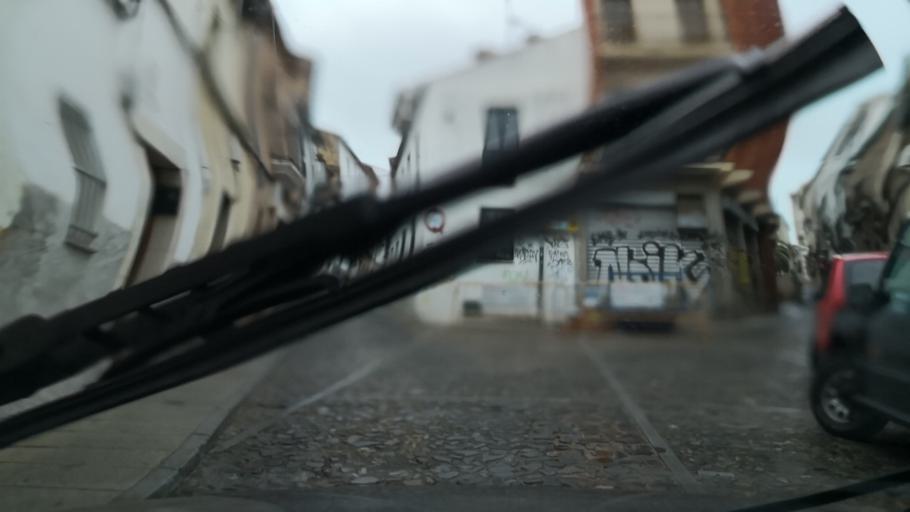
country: ES
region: Extremadura
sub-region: Provincia de Caceres
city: Caceres
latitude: 39.4780
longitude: -6.3693
